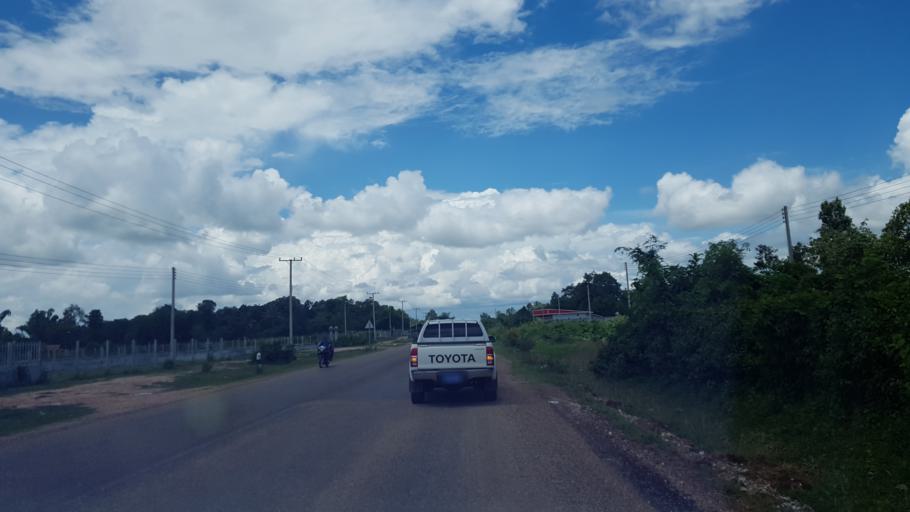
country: LA
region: Vientiane
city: Vientiane
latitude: 18.1148
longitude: 102.5869
